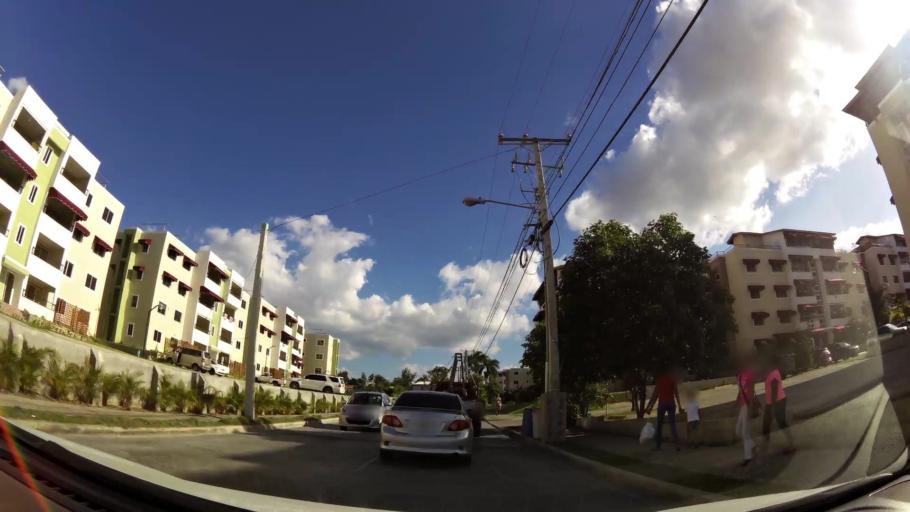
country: DO
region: Nacional
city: Santo Domingo
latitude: 18.5094
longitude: -69.9798
